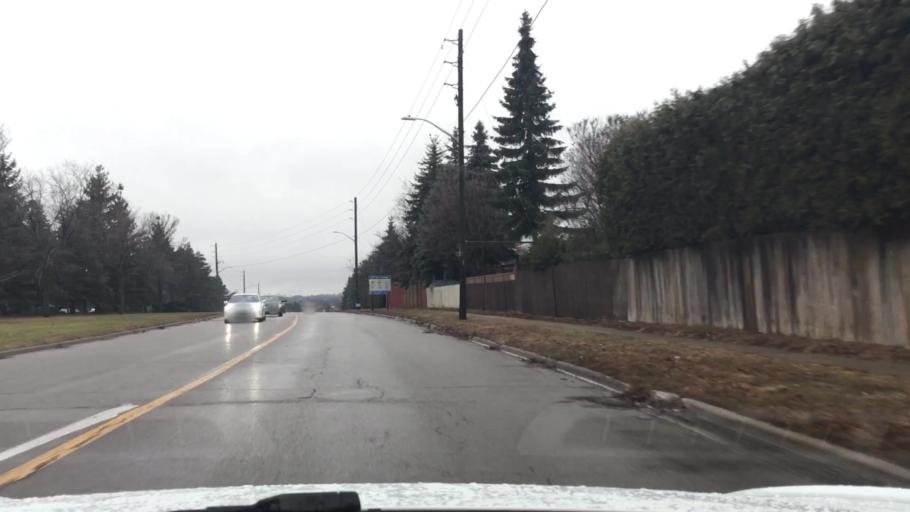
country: CA
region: Ontario
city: Oshawa
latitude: 43.8992
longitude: -78.8112
